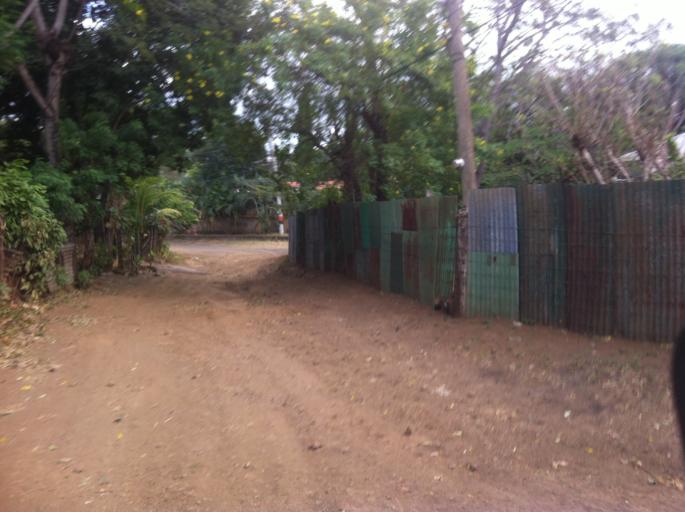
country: NI
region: Managua
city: Ciudad Sandino
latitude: 12.0840
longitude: -86.3262
